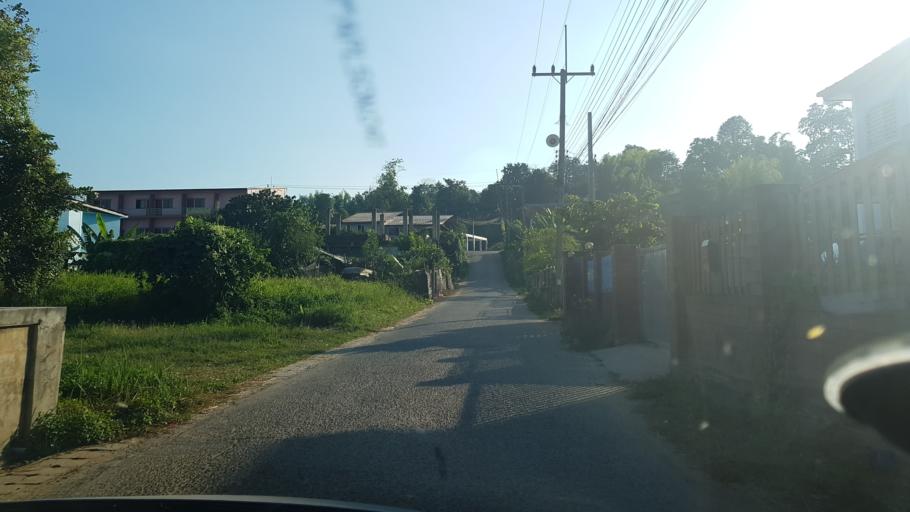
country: TH
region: Chiang Rai
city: Chiang Rai
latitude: 19.9439
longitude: 99.8046
